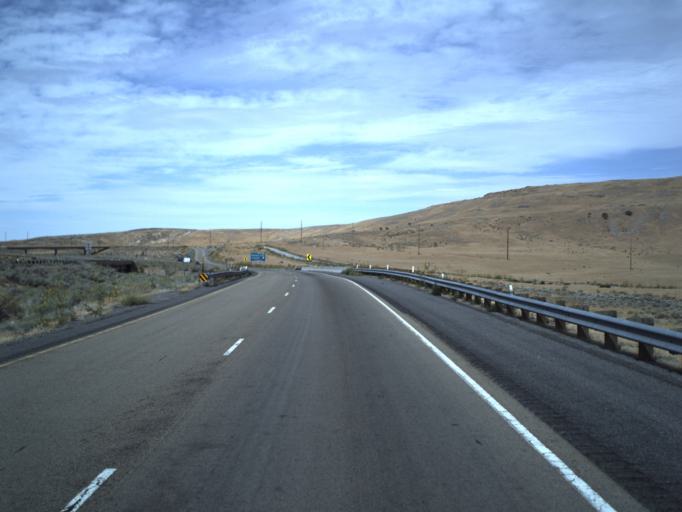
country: US
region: Utah
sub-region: Tooele County
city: Grantsville
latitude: 40.8230
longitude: -112.8945
